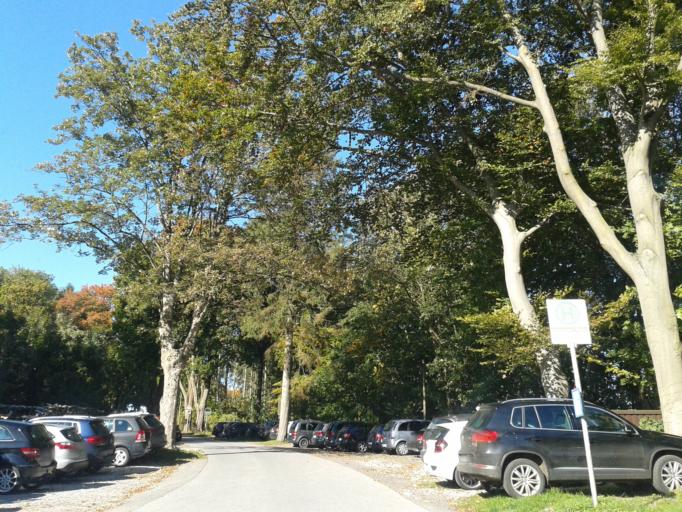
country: DE
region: North Rhine-Westphalia
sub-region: Regierungsbezirk Detmold
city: Paderborn
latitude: 51.6877
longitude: 8.7920
